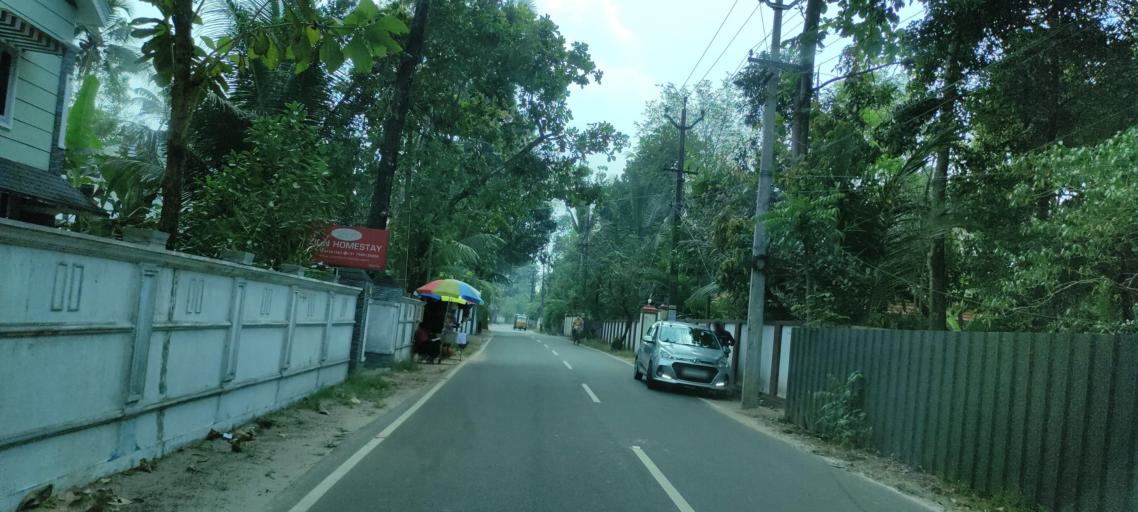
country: IN
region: Kerala
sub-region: Alappuzha
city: Alleppey
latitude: 9.5688
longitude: 76.3355
